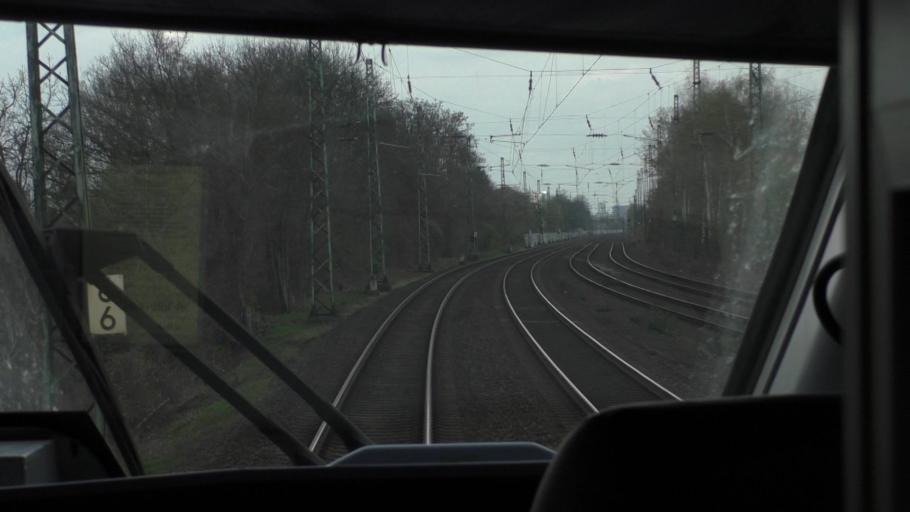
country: DE
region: North Rhine-Westphalia
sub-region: Regierungsbezirk Koln
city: Neustadt/Sued
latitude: 50.8991
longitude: 6.9237
